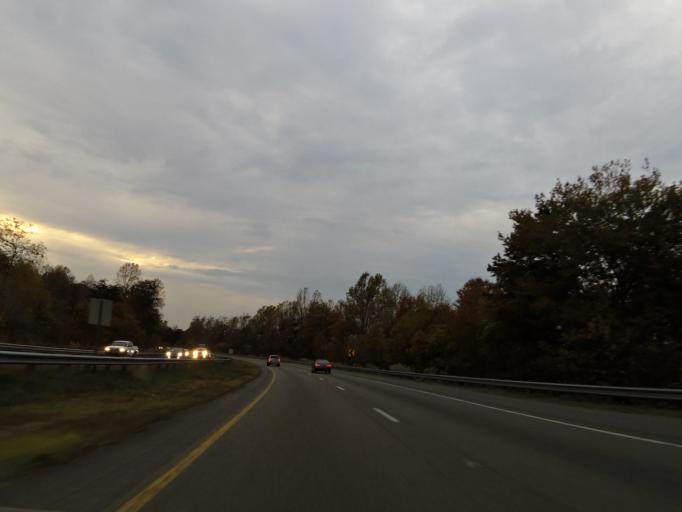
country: US
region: North Carolina
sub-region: Burke County
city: Connelly Springs
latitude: 35.7364
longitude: -81.5126
